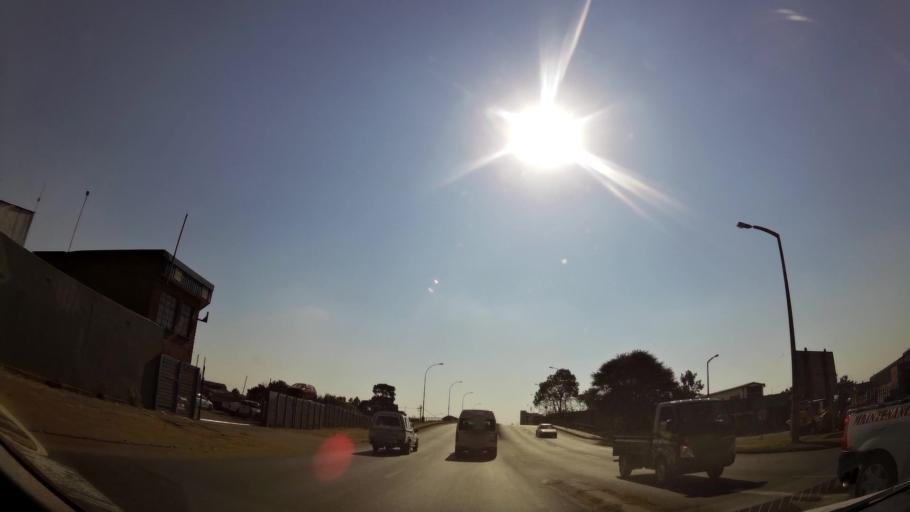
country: ZA
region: Gauteng
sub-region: Ekurhuleni Metropolitan Municipality
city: Benoni
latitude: -26.2029
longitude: 28.3033
